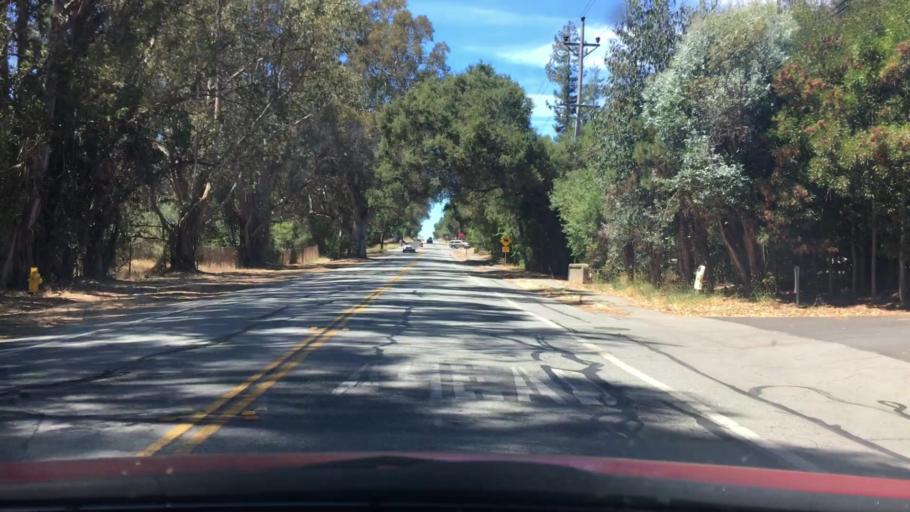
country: US
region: California
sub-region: San Mateo County
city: Emerald Lake Hills
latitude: 37.4472
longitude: -122.2732
